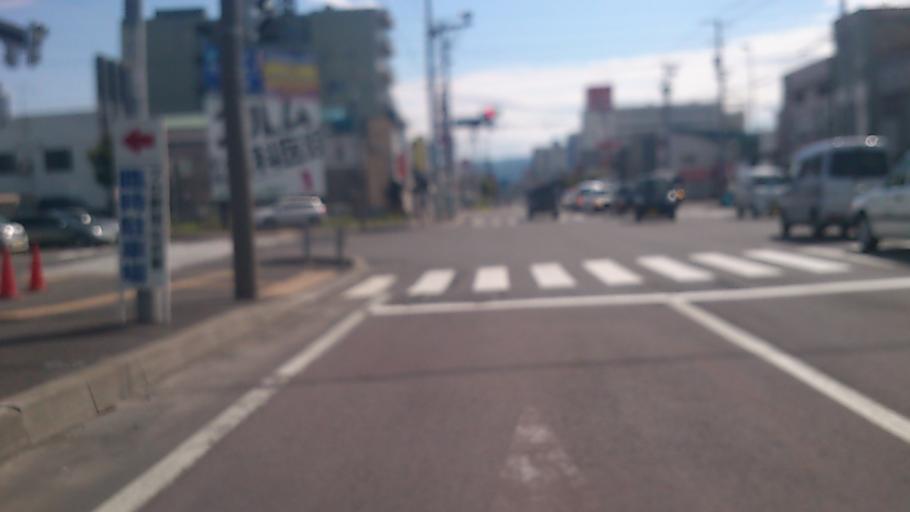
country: JP
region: Hokkaido
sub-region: Asahikawa-shi
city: Asahikawa
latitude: 43.7869
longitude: 142.3636
